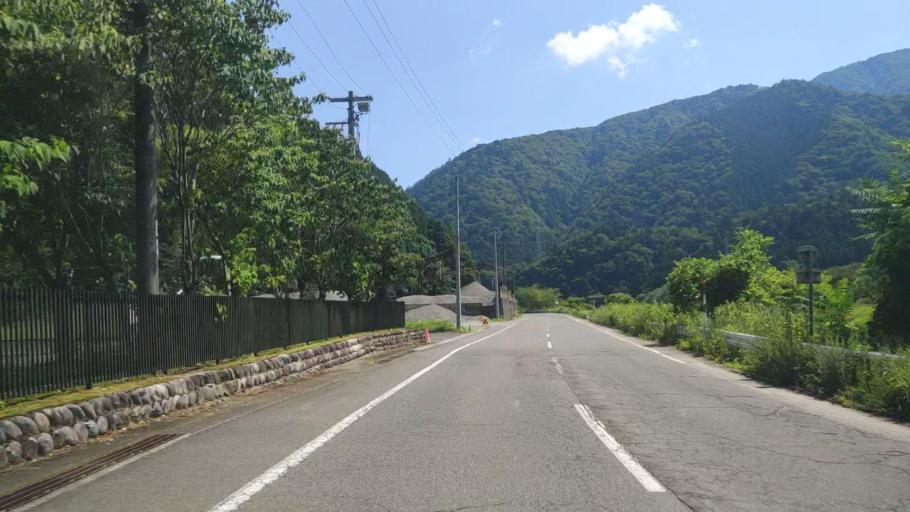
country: JP
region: Gifu
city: Godo
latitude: 35.6180
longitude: 136.6235
